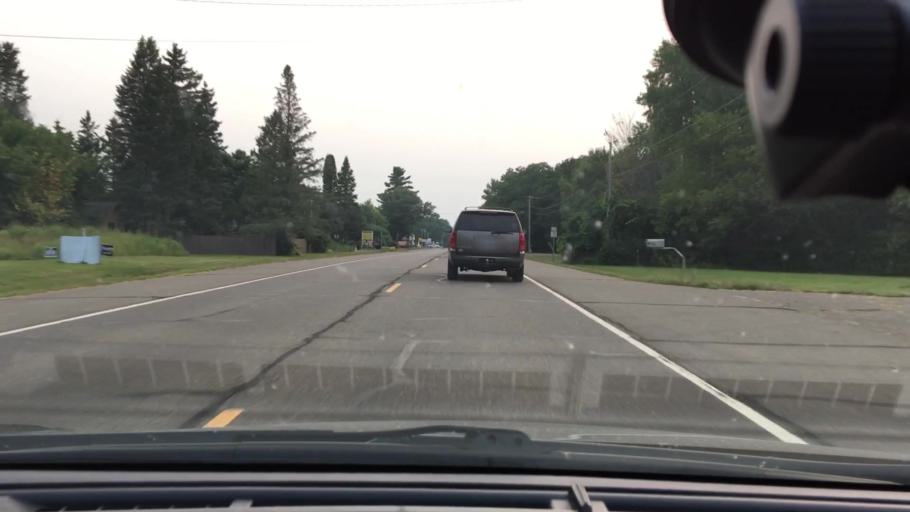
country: US
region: Minnesota
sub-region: Crow Wing County
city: Crosby
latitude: 46.4880
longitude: -93.9310
